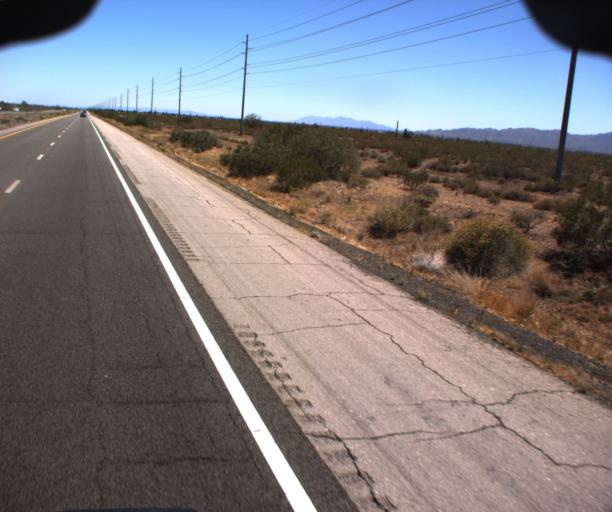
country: US
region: Arizona
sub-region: Maricopa County
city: Wickenburg
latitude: 33.8022
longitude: -112.5601
